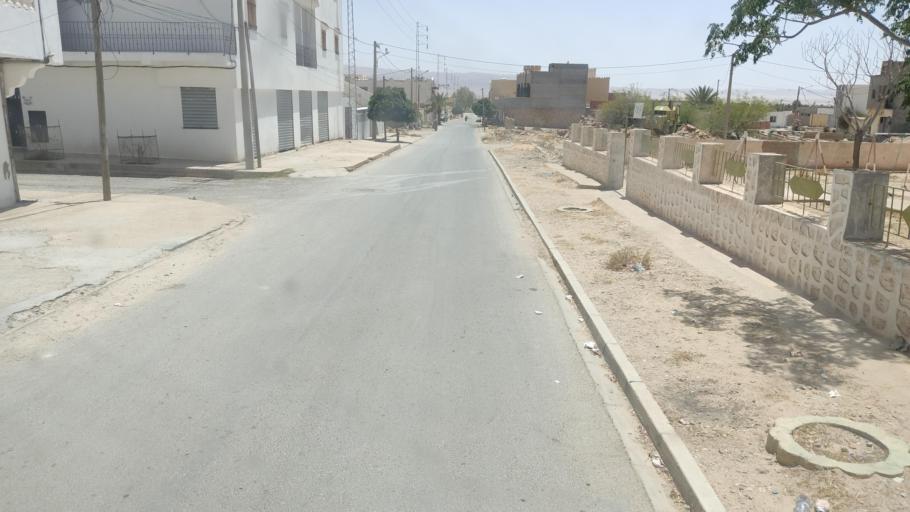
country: TN
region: Gafsa
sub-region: Gafsa Municipality
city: Gafsa
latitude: 34.3401
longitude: 8.9423
